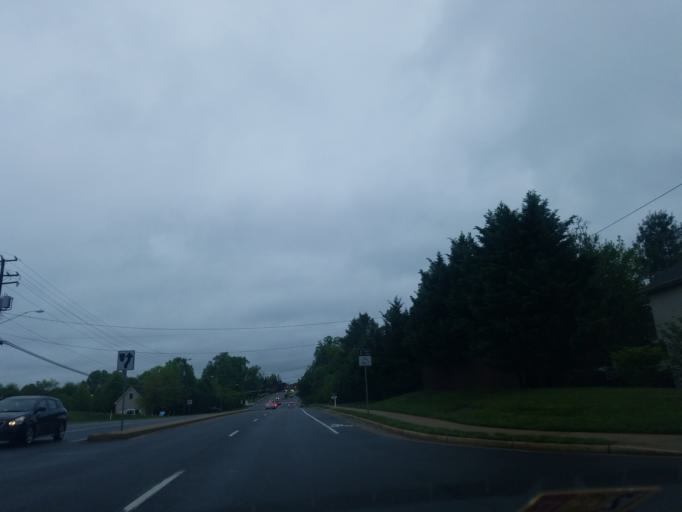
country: US
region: Virginia
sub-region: Fairfax County
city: Herndon
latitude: 38.9884
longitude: -77.3771
